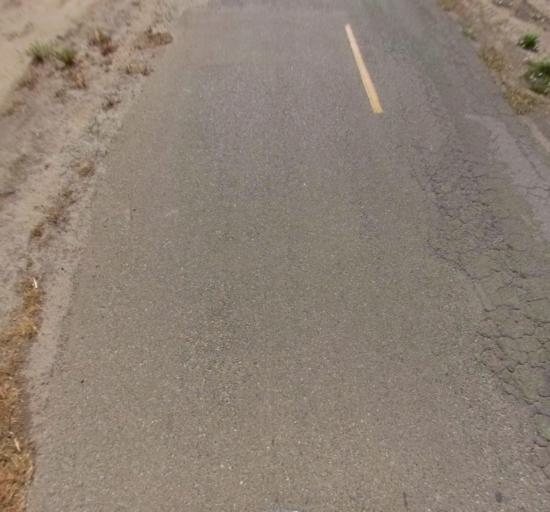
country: US
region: California
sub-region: Madera County
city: Fairmead
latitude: 37.0110
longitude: -120.2871
